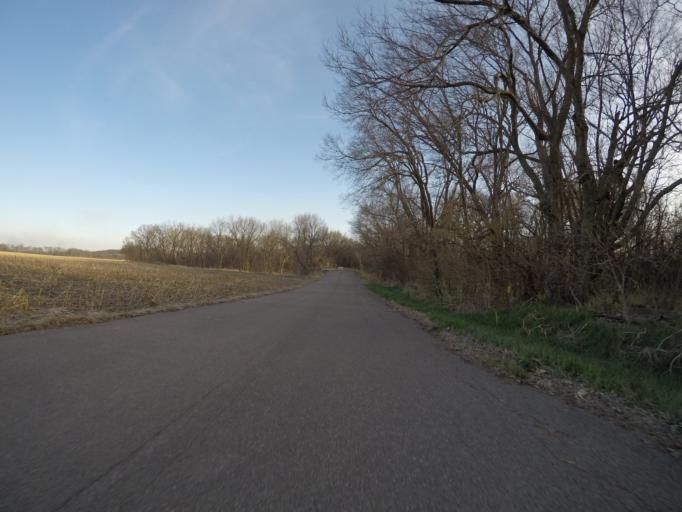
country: US
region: Kansas
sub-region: Riley County
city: Ogden
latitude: 39.2196
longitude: -96.7101
